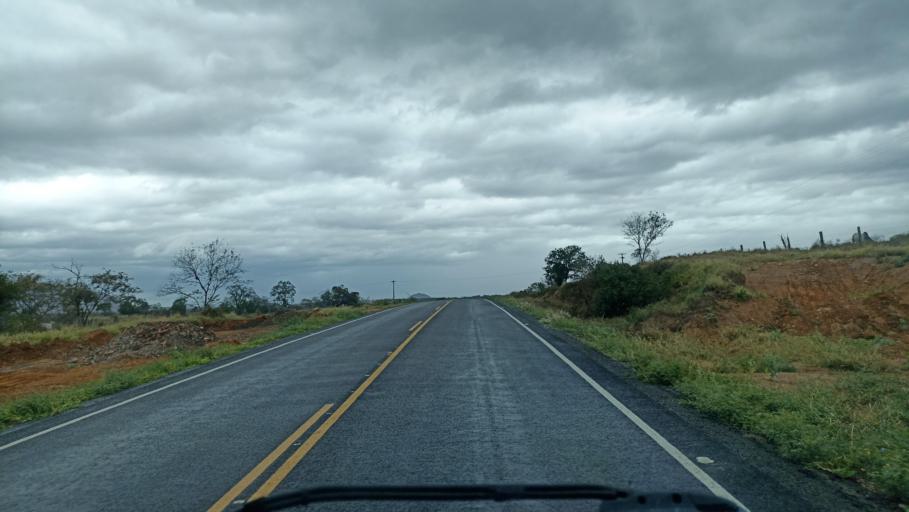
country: BR
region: Bahia
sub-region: Iacu
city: Iacu
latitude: -12.9668
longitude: -40.4918
